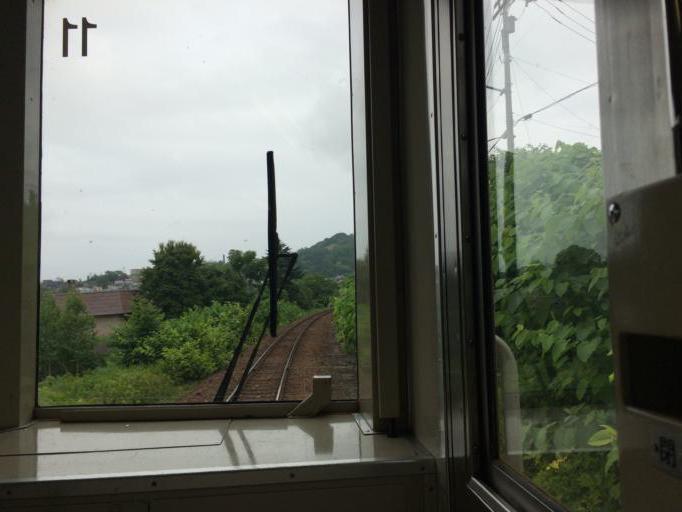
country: JP
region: Hokkaido
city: Otaru
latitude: 43.2082
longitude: 140.9761
